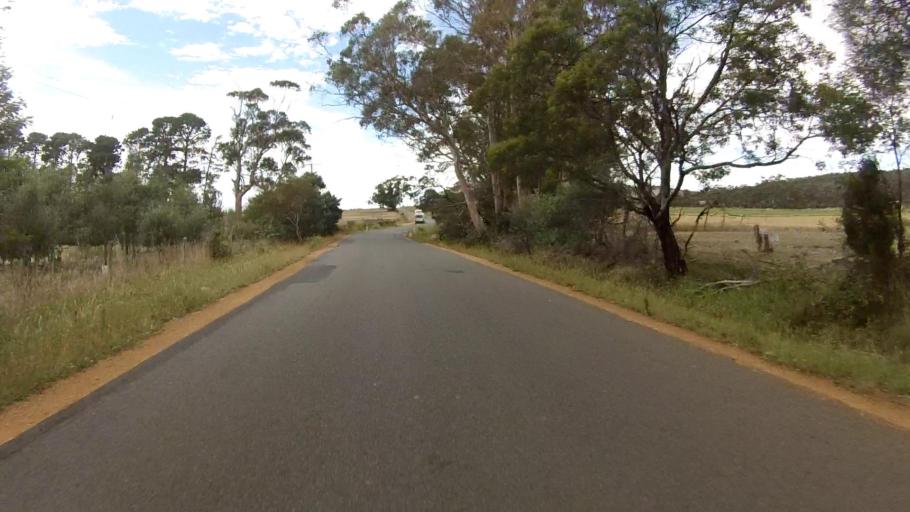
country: AU
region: Tasmania
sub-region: Clarence
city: Lindisfarne
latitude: -42.7535
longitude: 147.3783
